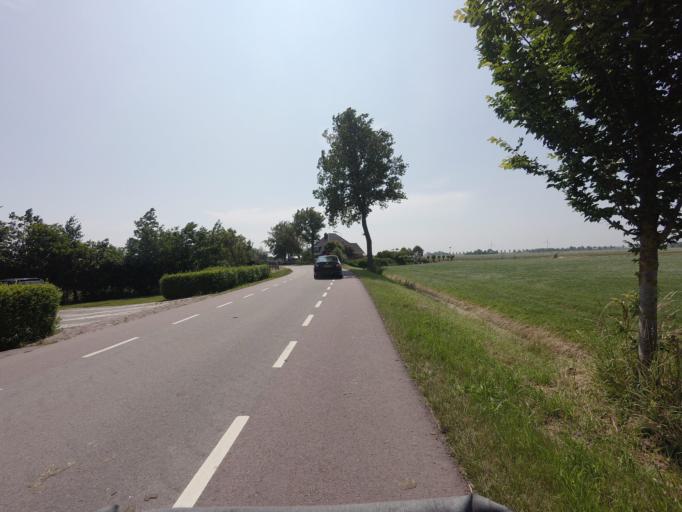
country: NL
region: North Holland
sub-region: Gemeente Opmeer
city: Opmeer
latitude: 52.6845
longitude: 4.9441
